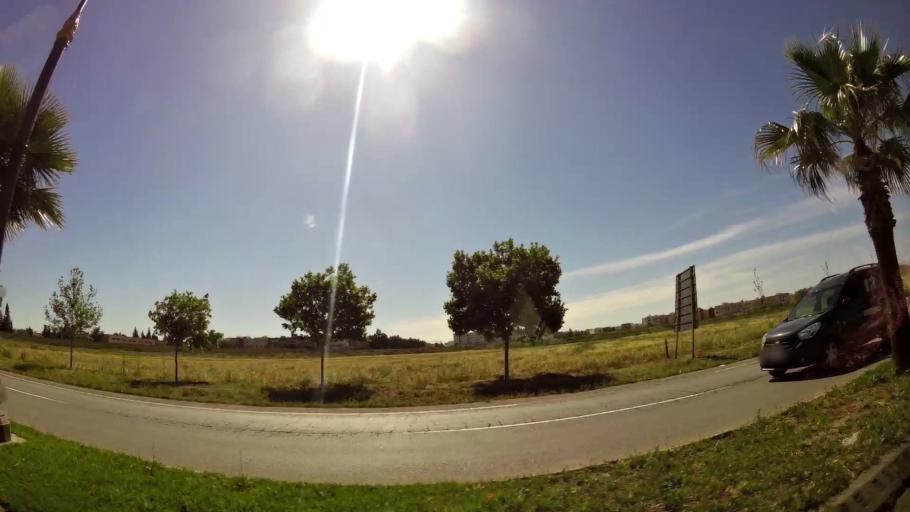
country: MA
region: Fes-Boulemane
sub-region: Fes
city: Fes
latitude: 34.0142
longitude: -5.0196
